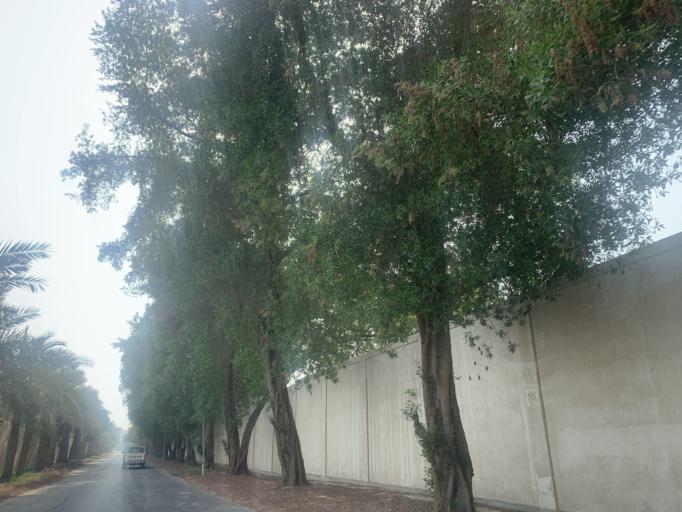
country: BH
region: Manama
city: Jidd Hafs
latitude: 26.2132
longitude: 50.4738
